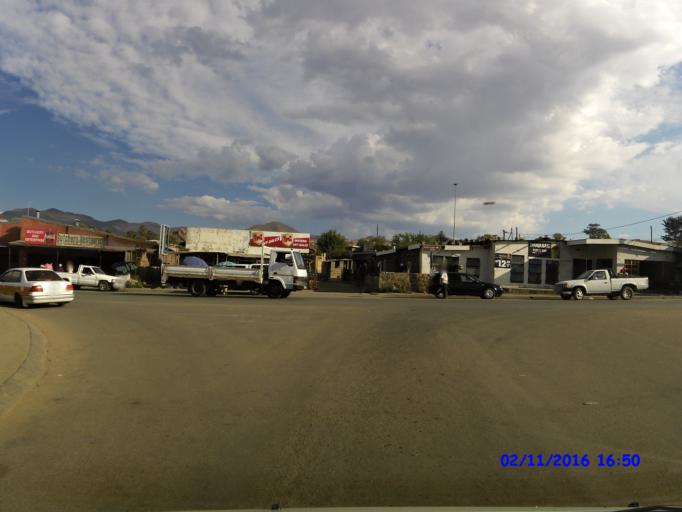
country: LS
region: Butha-Buthe
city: Butha-Buthe
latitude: -28.7674
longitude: 28.2523
